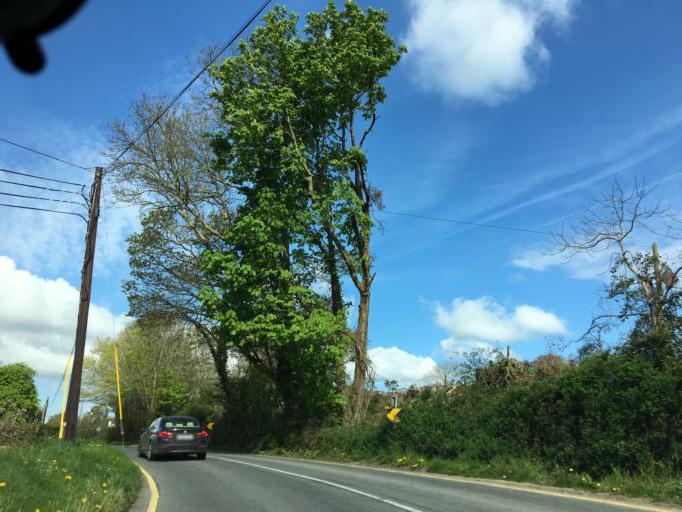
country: IE
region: Leinster
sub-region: Loch Garman
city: New Ross
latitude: 52.4219
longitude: -6.9334
